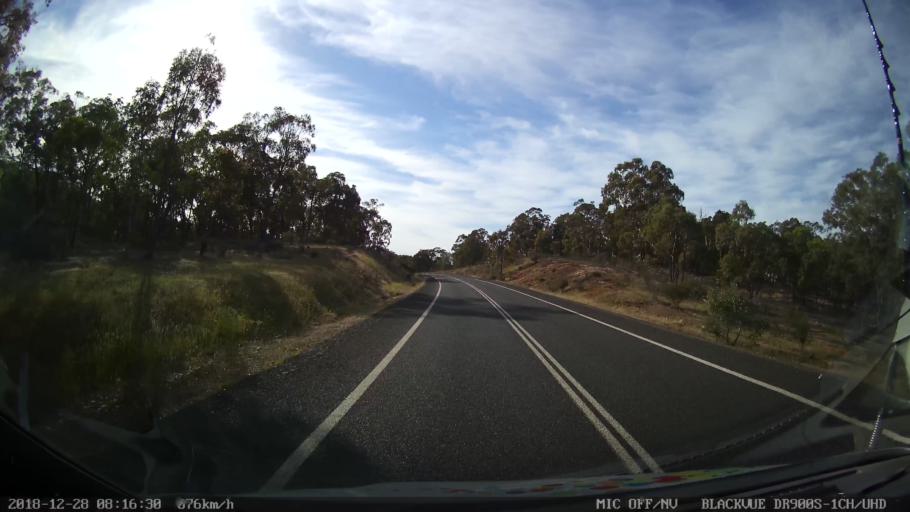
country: AU
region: New South Wales
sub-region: Blayney
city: Blayney
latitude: -33.8343
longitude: 149.3297
